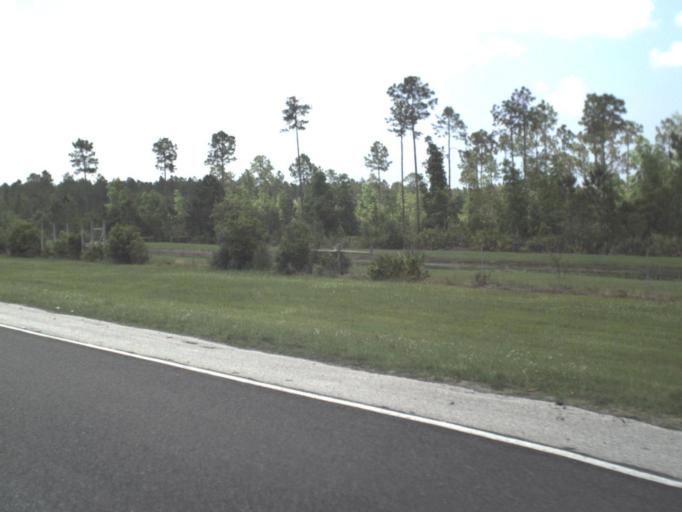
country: US
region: Florida
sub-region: Saint Johns County
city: Saint Augustine Shores
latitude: 29.7530
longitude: -81.3484
